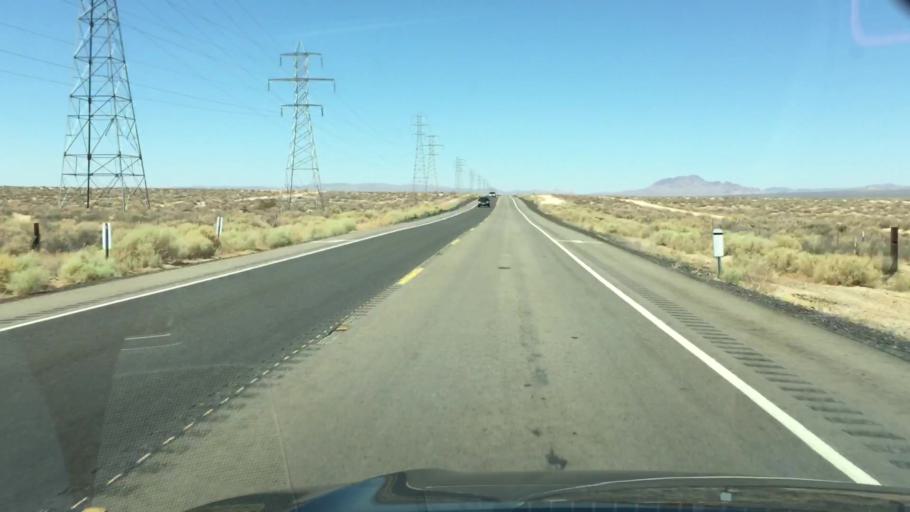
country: US
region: California
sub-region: Kern County
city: Boron
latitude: 35.1118
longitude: -117.5749
